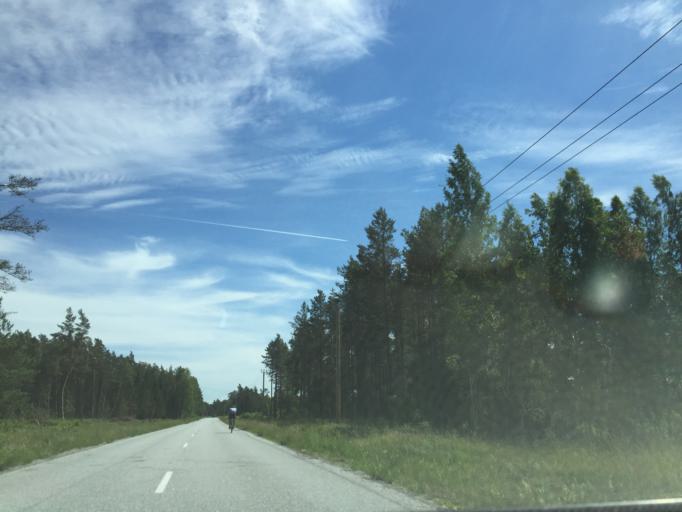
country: LV
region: Talsu Rajons
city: Valdemarpils
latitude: 57.6218
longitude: 22.5808
